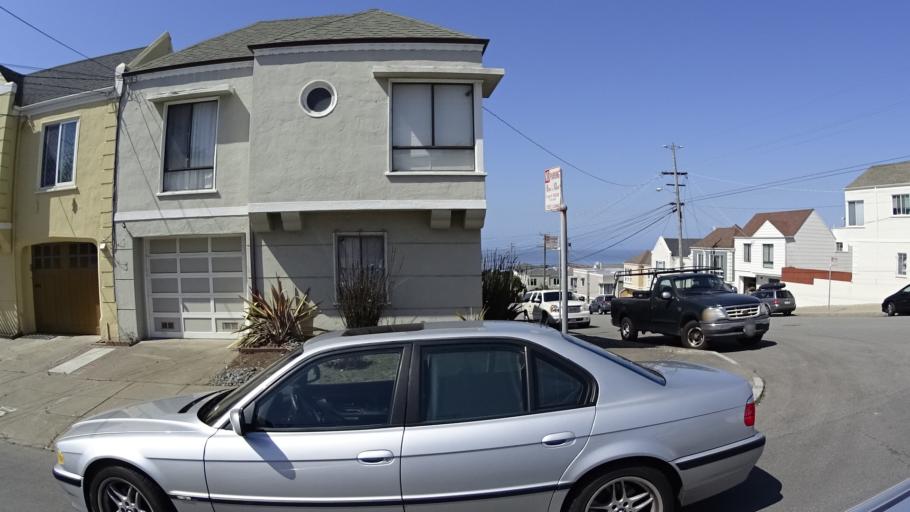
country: US
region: California
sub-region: San Mateo County
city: Daly City
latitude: 37.7500
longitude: -122.4869
